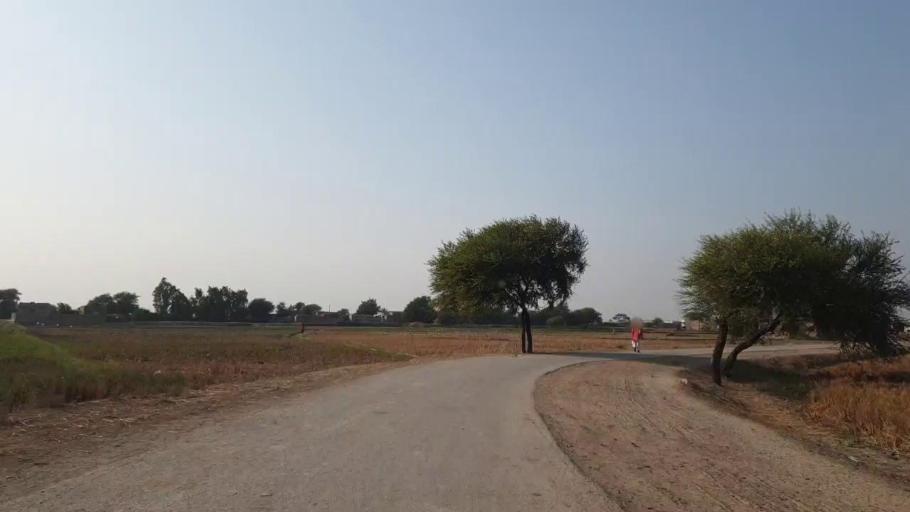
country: PK
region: Sindh
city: Bulri
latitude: 24.9970
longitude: 68.3798
